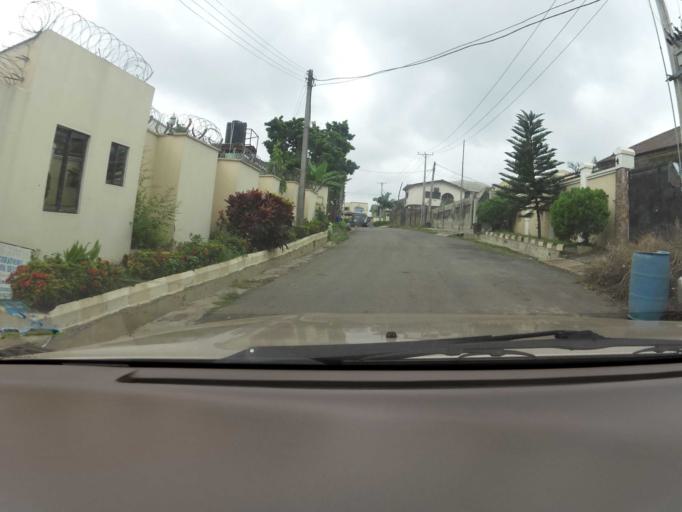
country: NG
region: Oyo
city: Ibadan
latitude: 7.4264
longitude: 3.9407
